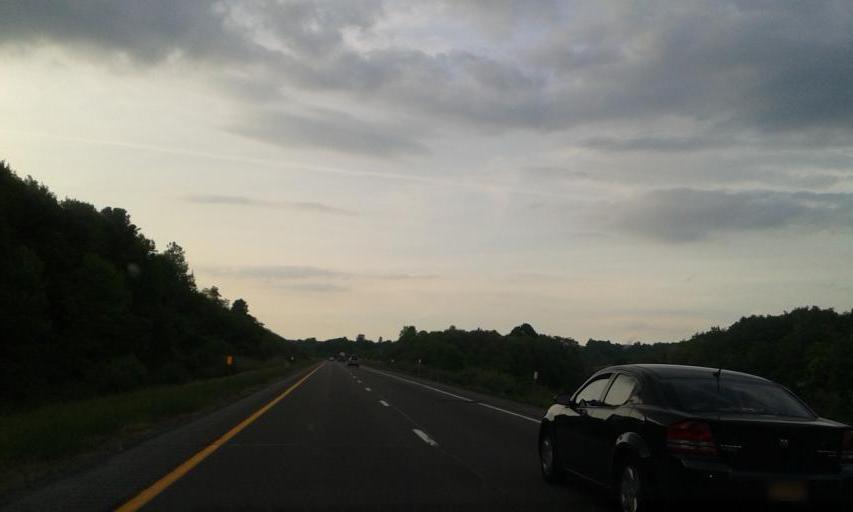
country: US
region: New York
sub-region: Broome County
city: Chenango Bridge
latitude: 42.2634
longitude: -75.9193
